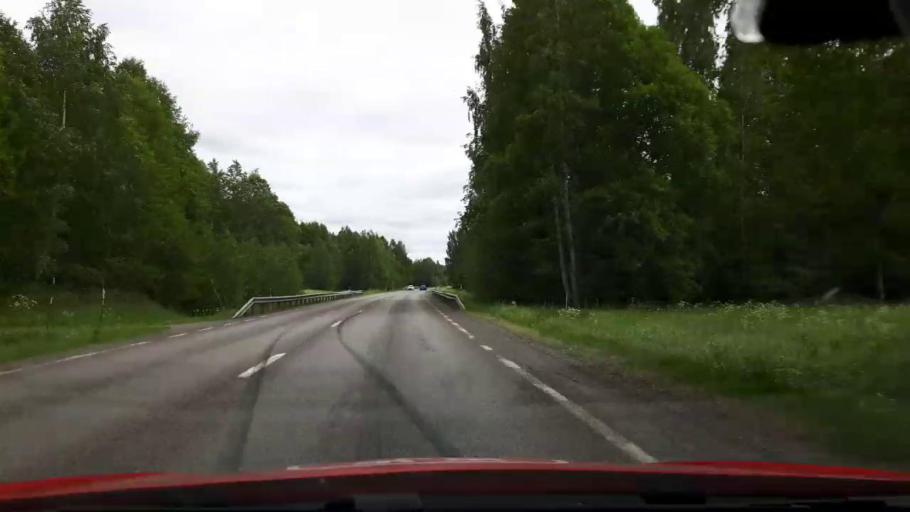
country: SE
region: Jaemtland
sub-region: Ragunda Kommun
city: Hammarstrand
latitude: 63.1289
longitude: 16.3544
